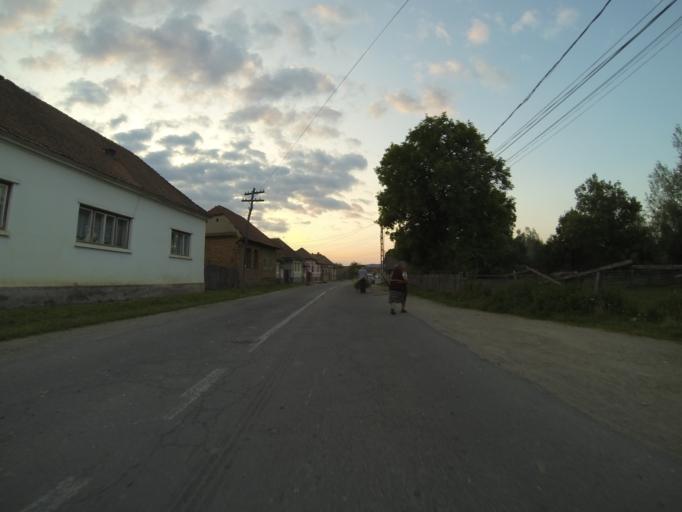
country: RO
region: Brasov
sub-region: Comuna Sinca Noua
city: Sinca Noua
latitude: 45.7055
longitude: 25.2457
